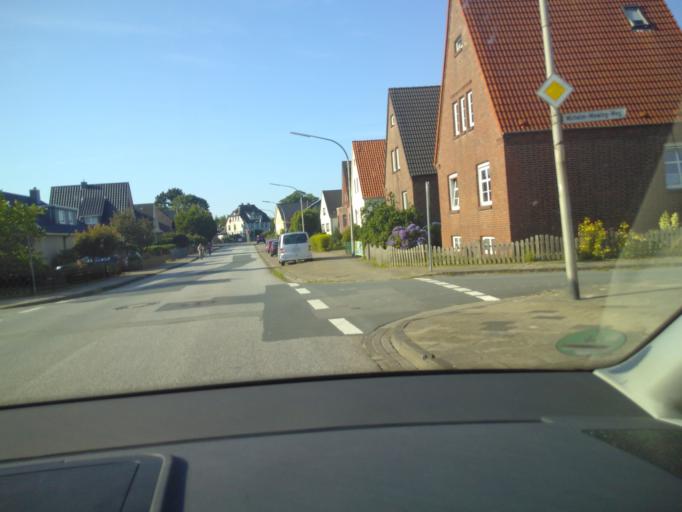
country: DE
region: Lower Saxony
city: Cuxhaven
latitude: 53.8723
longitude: 8.6536
